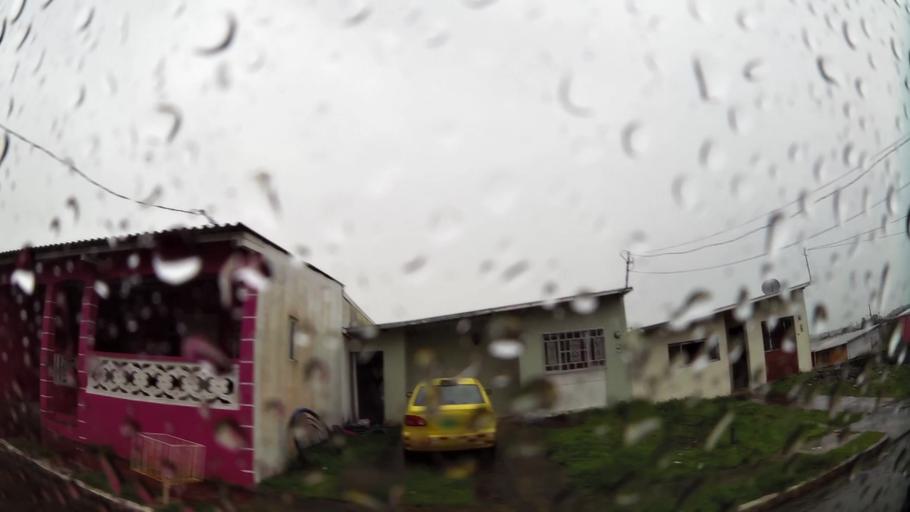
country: PA
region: Colon
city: Puerto Pilon
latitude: 9.3576
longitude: -79.7895
